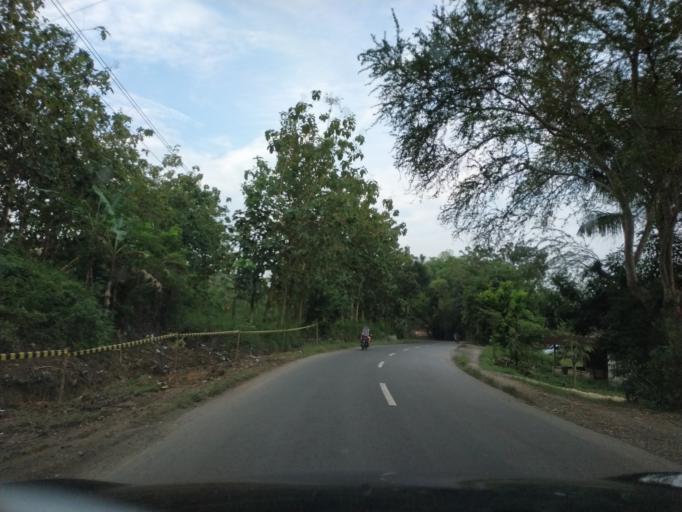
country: ID
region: Central Java
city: Medang
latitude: -6.9040
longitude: 111.4428
